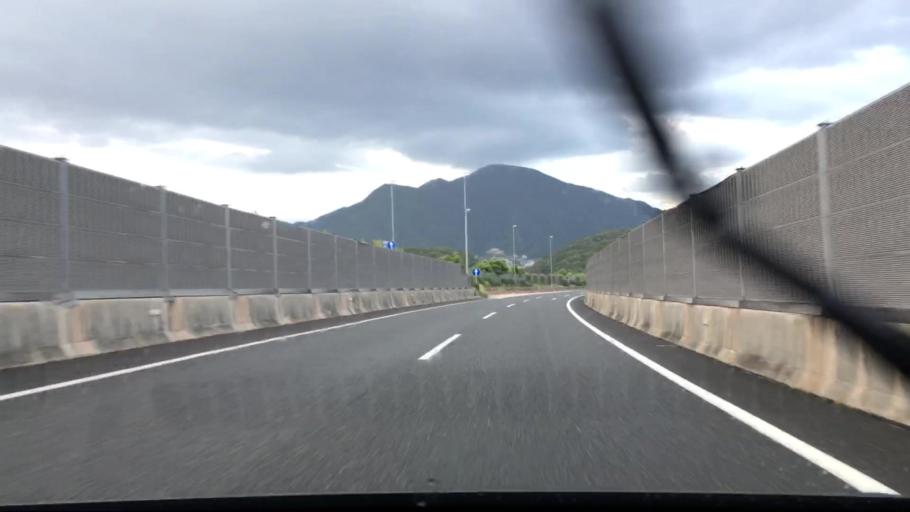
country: JP
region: Fukuoka
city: Kitakyushu
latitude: 33.8206
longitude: 130.8868
